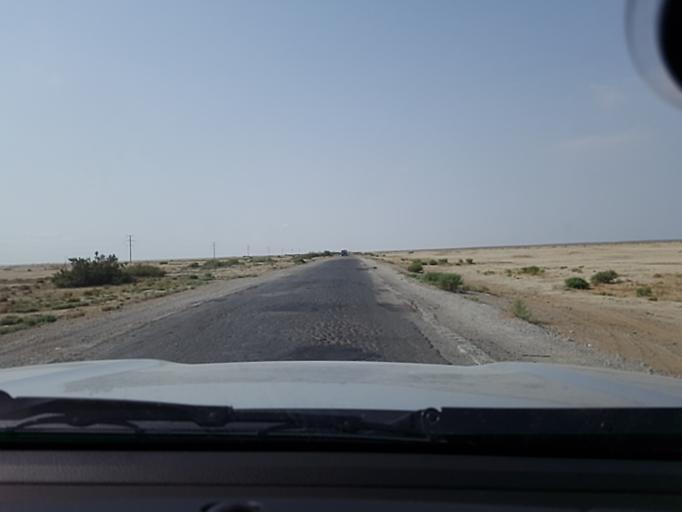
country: TM
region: Balkan
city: Gumdag
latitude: 38.9801
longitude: 54.5874
